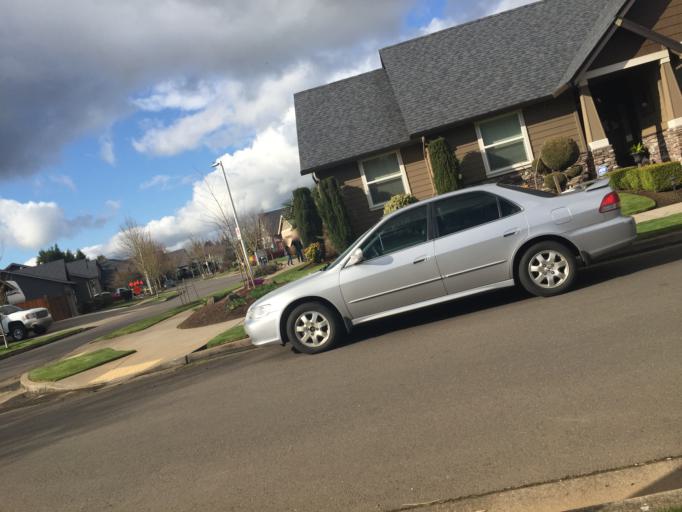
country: US
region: Oregon
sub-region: Lane County
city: Eugene
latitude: 44.0995
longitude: -123.1548
